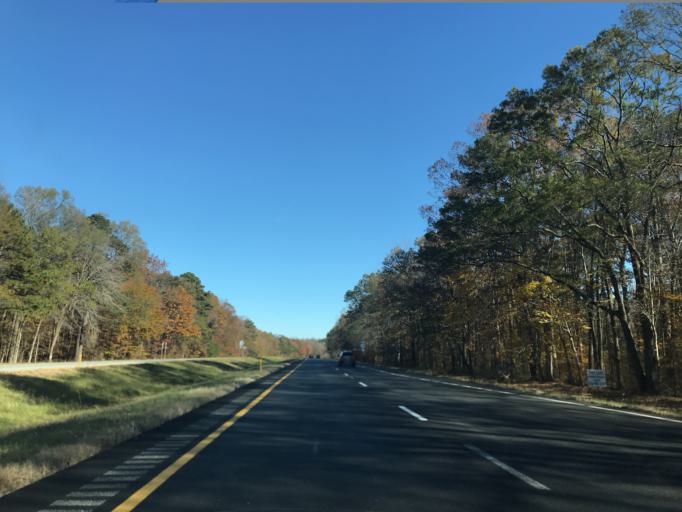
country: US
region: Maryland
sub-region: Queen Anne's County
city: Centreville
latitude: 39.0080
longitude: -76.1117
